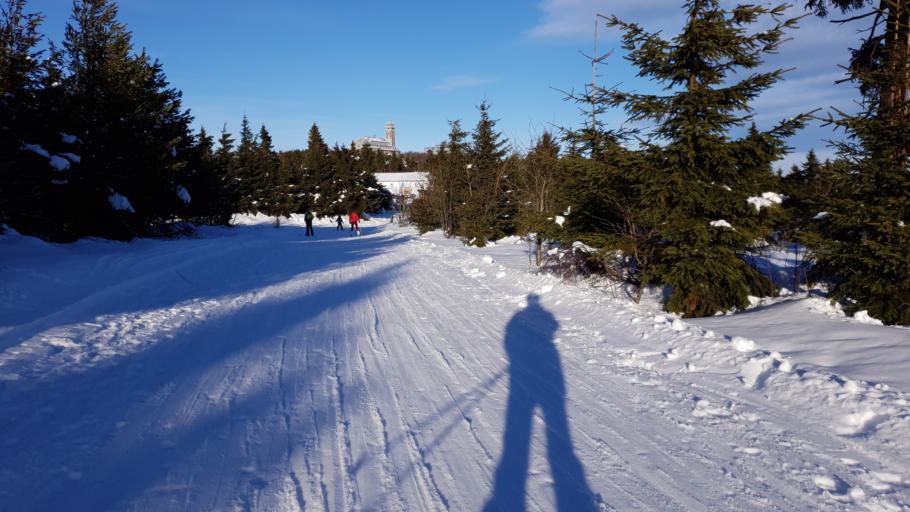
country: DE
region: Saxony
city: Kurort Oberwiesenthal
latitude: 50.4243
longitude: 12.9519
